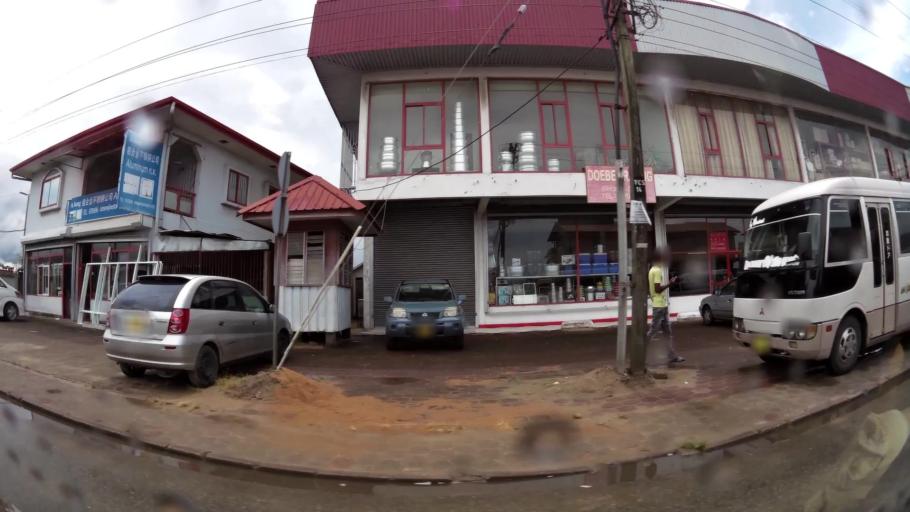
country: SR
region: Paramaribo
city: Paramaribo
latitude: 5.7949
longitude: -55.1902
